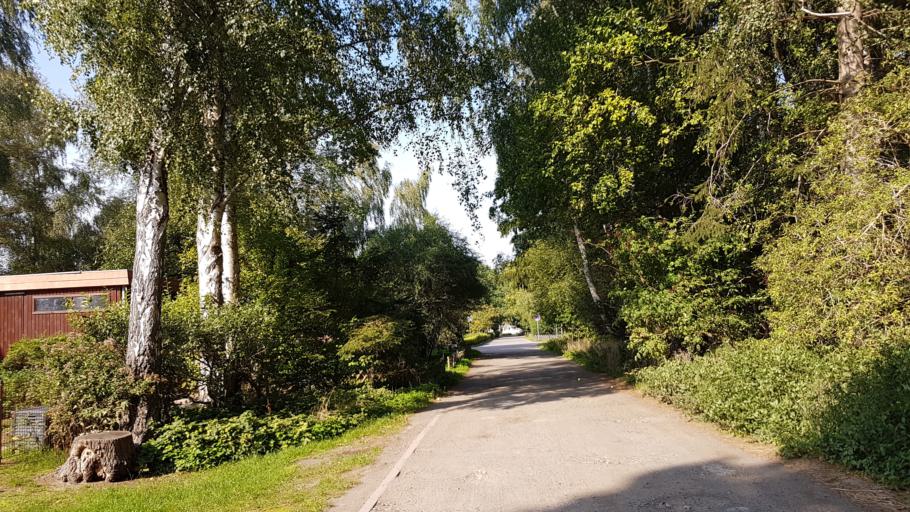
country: DE
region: Mecklenburg-Vorpommern
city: Glowe
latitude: 54.5659
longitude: 13.4593
